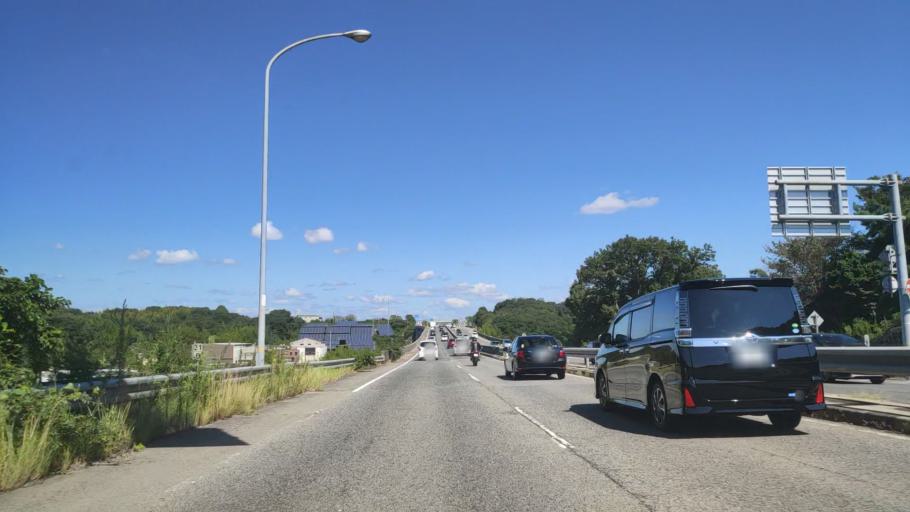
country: JP
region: Hyogo
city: Ono
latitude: 34.8318
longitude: 134.9488
